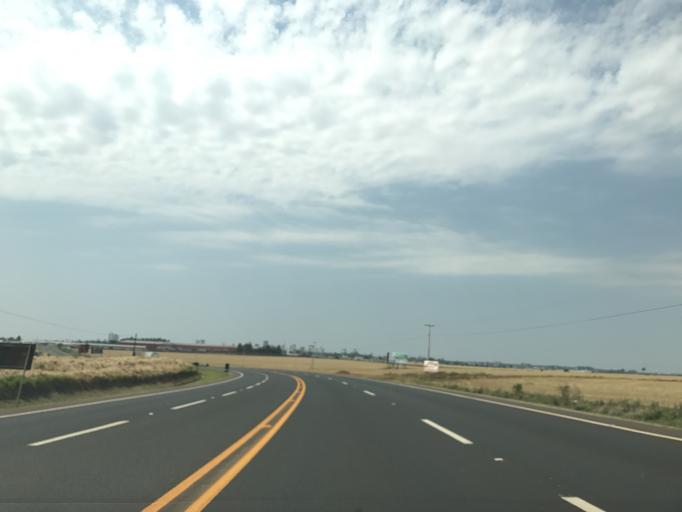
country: BR
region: Parana
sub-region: Arapongas
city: Arapongas
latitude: -23.4169
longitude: -51.4823
